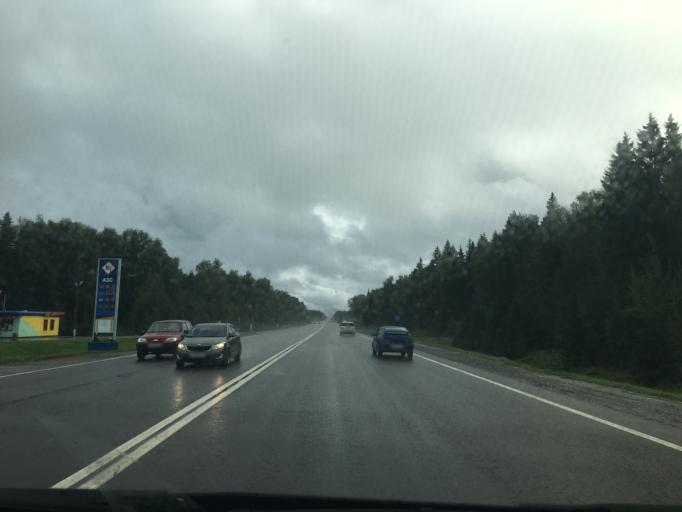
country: RU
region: Kaluga
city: Balabanovo
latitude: 55.1609
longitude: 36.6670
